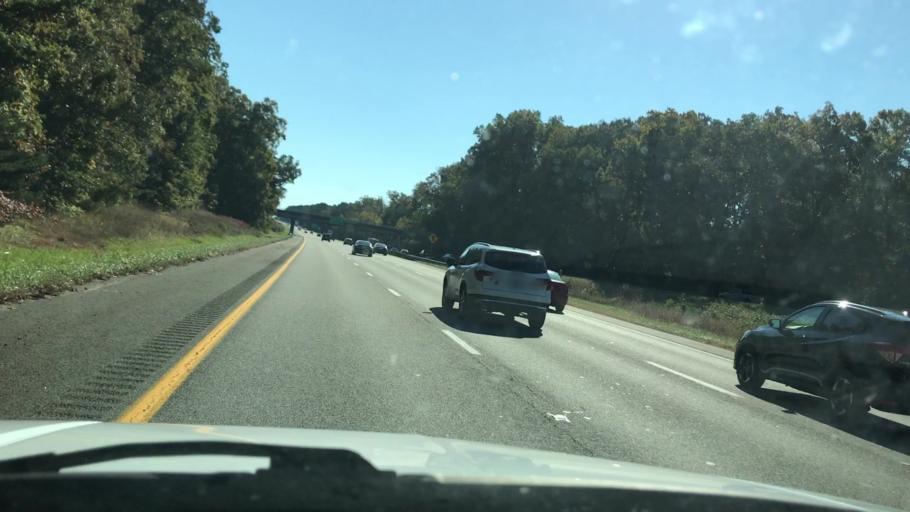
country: US
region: Virginia
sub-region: Henrico County
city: Short Pump
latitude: 37.6334
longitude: -77.5723
